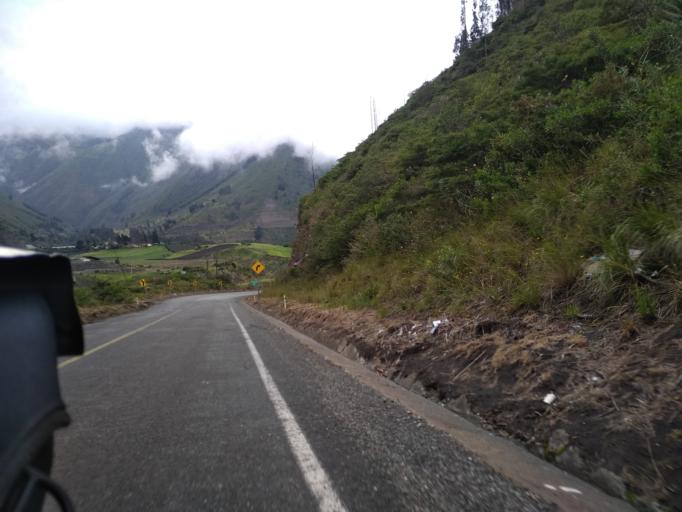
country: EC
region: Tungurahua
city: Banos
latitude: -1.5073
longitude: -78.5195
